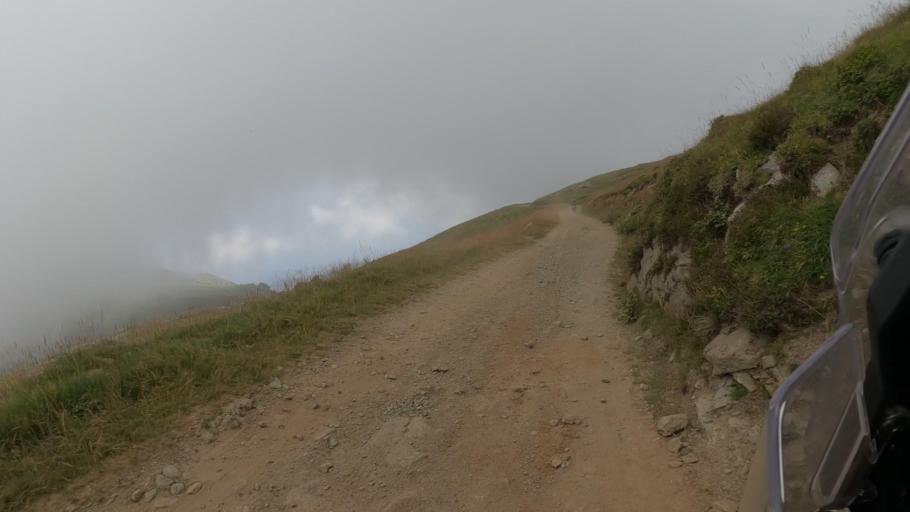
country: IT
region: Piedmont
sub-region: Provincia di Torino
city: Lemie
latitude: 45.1747
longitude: 7.2814
